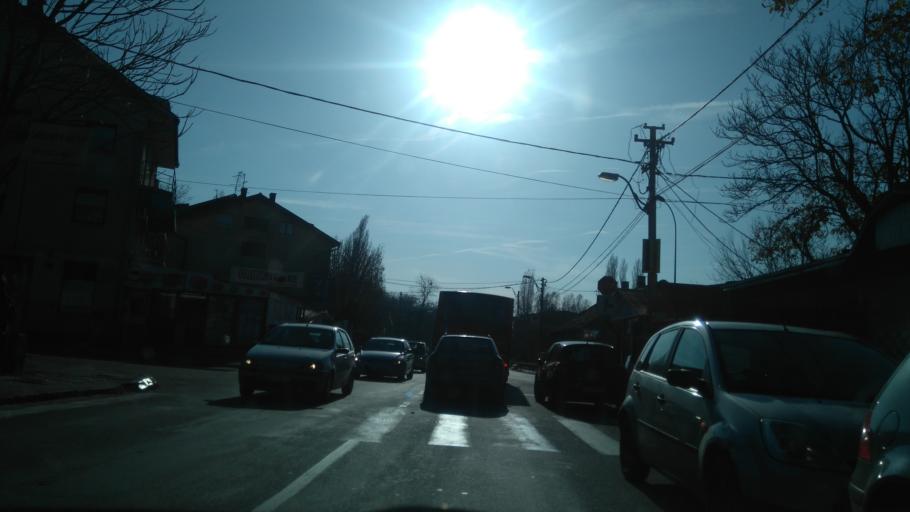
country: RS
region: Central Serbia
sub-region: Belgrade
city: Cukarica
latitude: 44.7551
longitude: 20.4041
